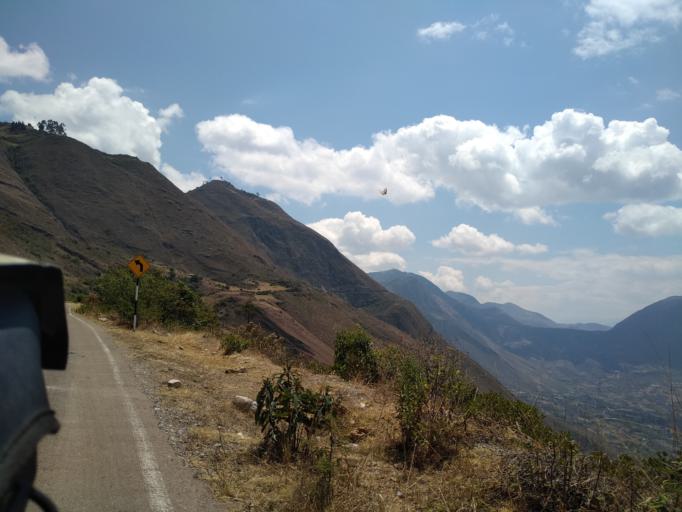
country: PE
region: Cajamarca
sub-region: Provincia de Celendin
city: Celendin
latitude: -6.8846
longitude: -78.1012
